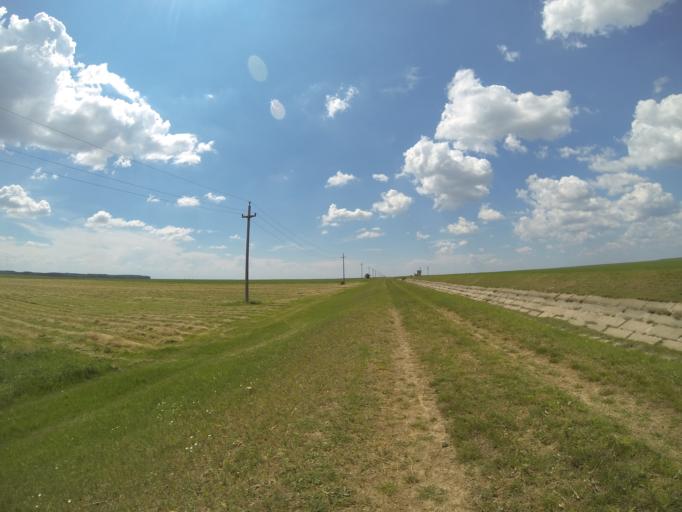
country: RO
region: Dolj
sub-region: Comuna Dranicu
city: Padea
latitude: 44.0115
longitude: 23.8370
